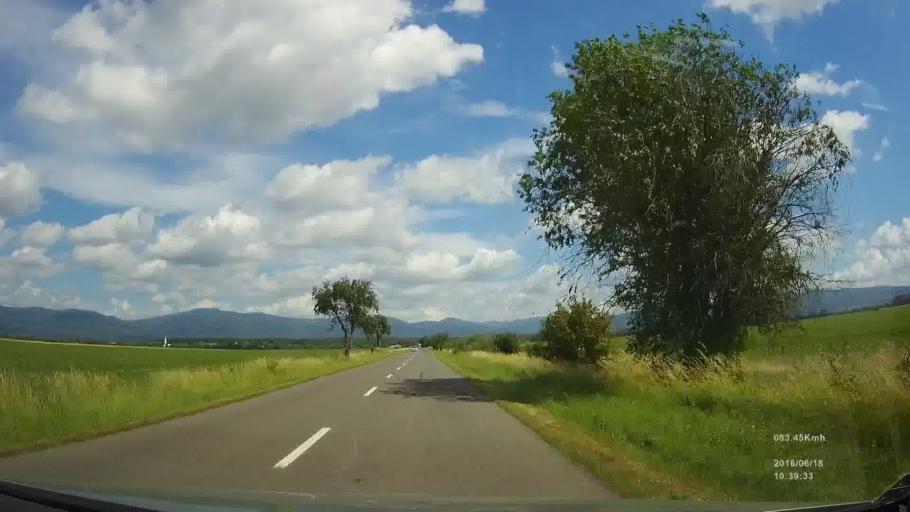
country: SK
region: Kosicky
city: Sobrance
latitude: 48.7744
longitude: 22.1272
